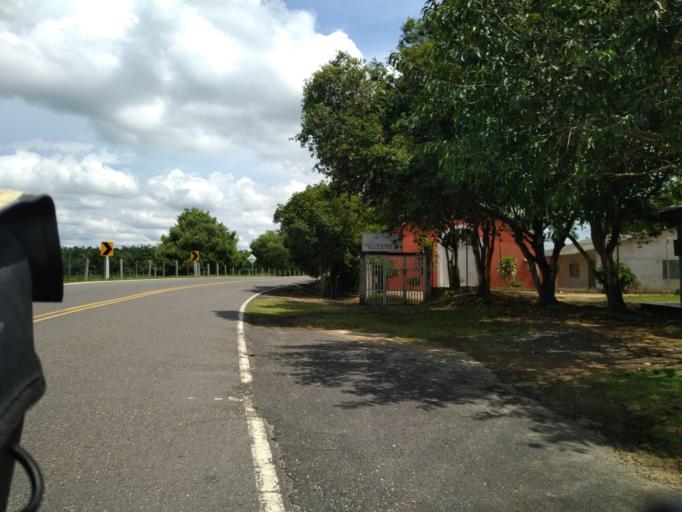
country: CO
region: Santander
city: Puerto Parra
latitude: 6.4929
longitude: -74.0475
